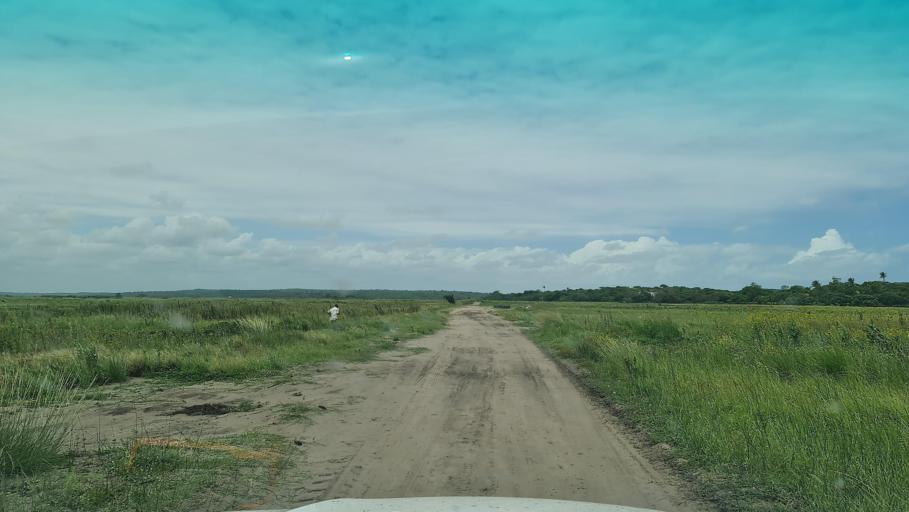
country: MZ
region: Maputo
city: Manhica
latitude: -25.5263
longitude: 32.8546
